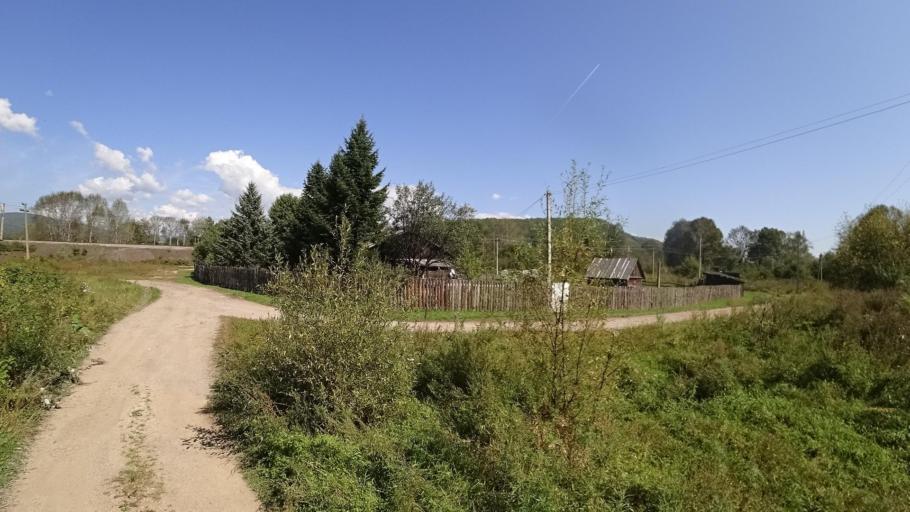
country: RU
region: Jewish Autonomous Oblast
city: Londoko
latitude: 49.0140
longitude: 132.2297
